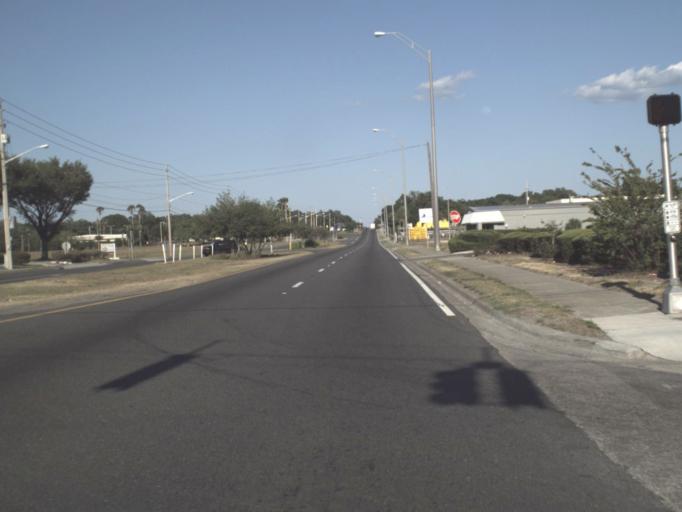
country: US
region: Florida
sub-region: Marion County
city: Ocala
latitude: 29.1862
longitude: -82.1770
